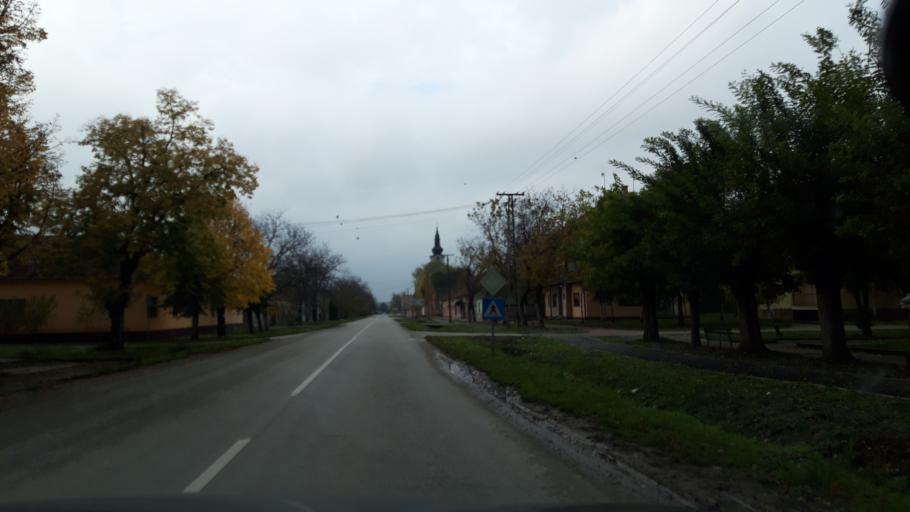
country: RS
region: Autonomna Pokrajina Vojvodina
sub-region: Severnobanatski Okrug
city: Kanjiza
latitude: 46.1254
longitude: 20.0961
